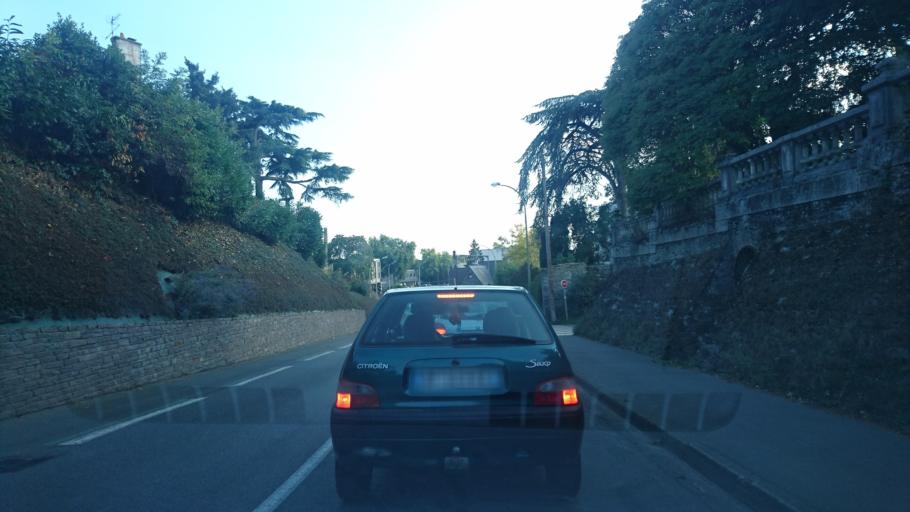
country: FR
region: Brittany
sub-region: Departement d'Ille-et-Vilaine
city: Redon
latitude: 47.6561
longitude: -2.0839
